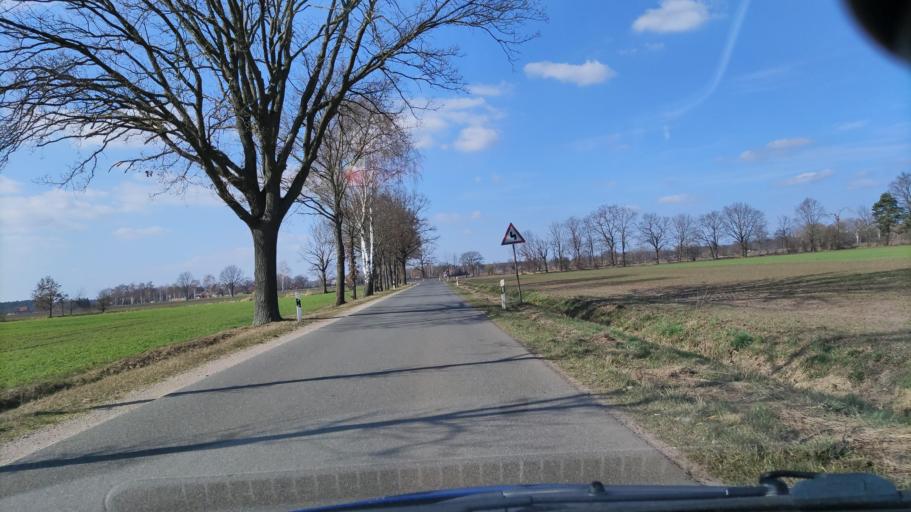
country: DE
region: Lower Saxony
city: Langendorf
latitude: 53.0492
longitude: 11.2362
